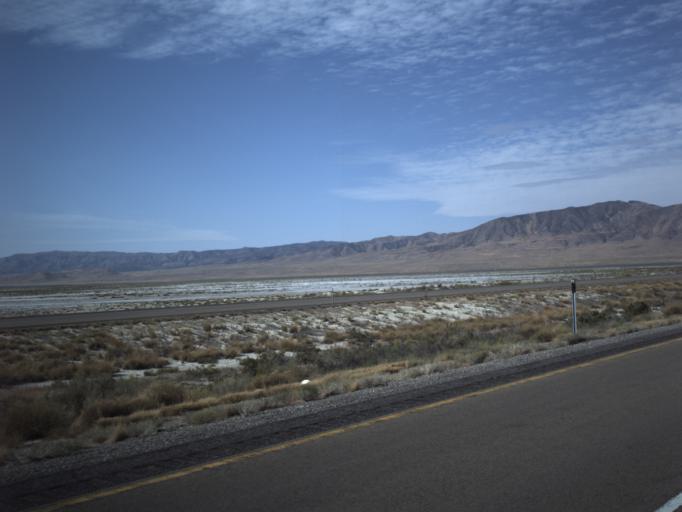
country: US
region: Utah
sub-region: Tooele County
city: Grantsville
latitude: 40.7575
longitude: -112.7663
